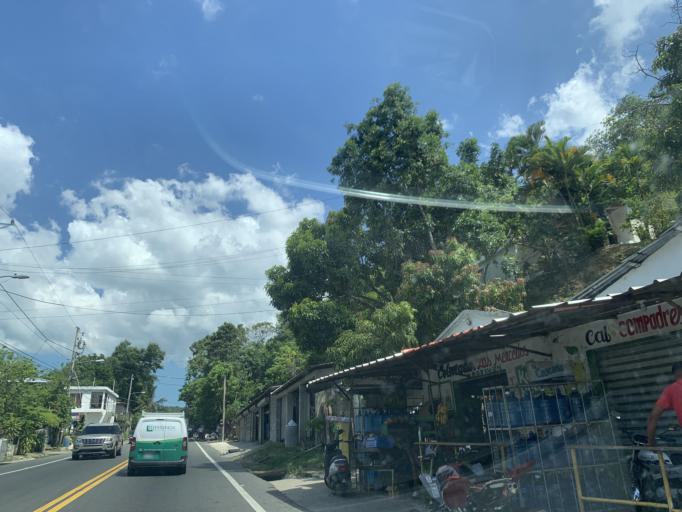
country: DO
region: Puerto Plata
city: Altamira
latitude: 19.6718
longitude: -70.8341
